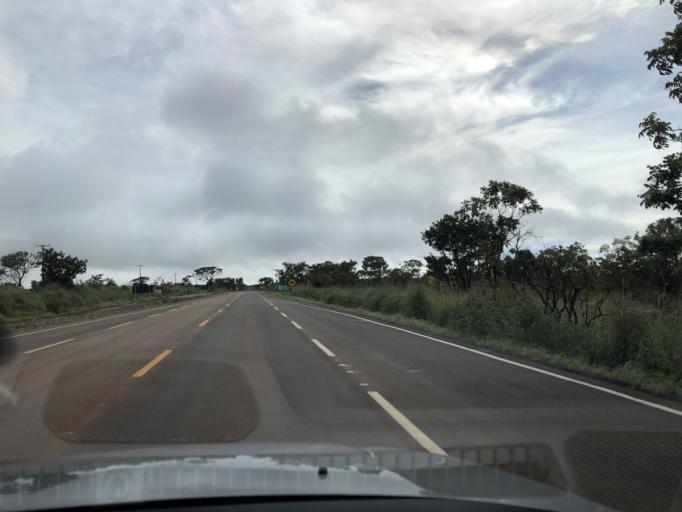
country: BR
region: Federal District
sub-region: Brasilia
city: Brasilia
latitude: -15.6193
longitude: -48.0586
